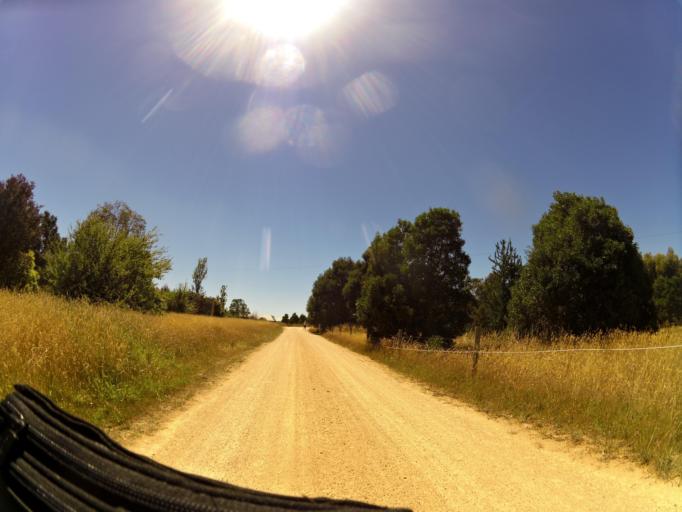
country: AU
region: Victoria
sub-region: Ballarat North
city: Delacombe
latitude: -37.7024
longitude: 143.6419
